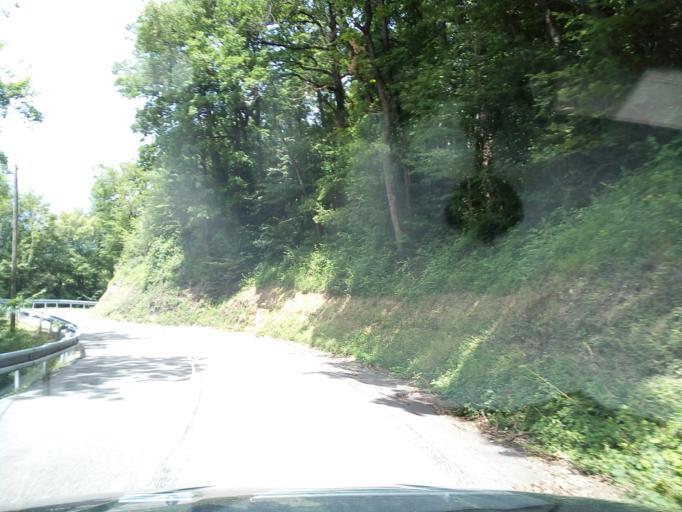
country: FR
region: Rhone-Alpes
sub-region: Departement de l'Isere
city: Saint-Martin-d'Heres
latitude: 45.1658
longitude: 5.7798
